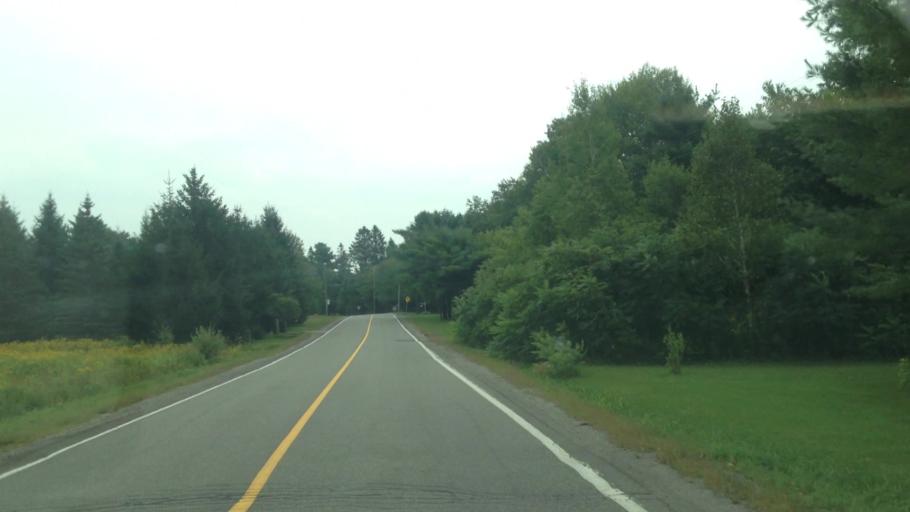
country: CA
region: Quebec
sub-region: Laurentides
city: Sainte-Sophie
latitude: 45.8640
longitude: -73.9088
